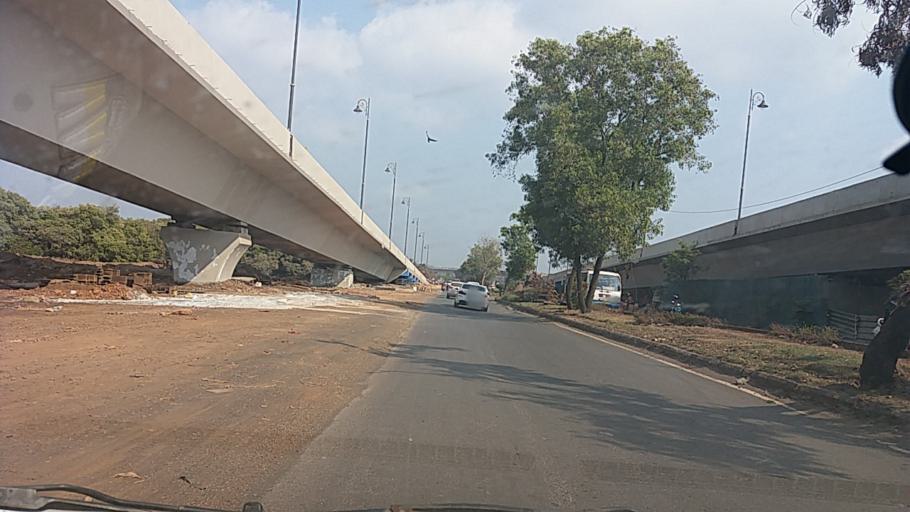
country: IN
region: Goa
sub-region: North Goa
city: Panaji
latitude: 15.4942
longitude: 73.8398
